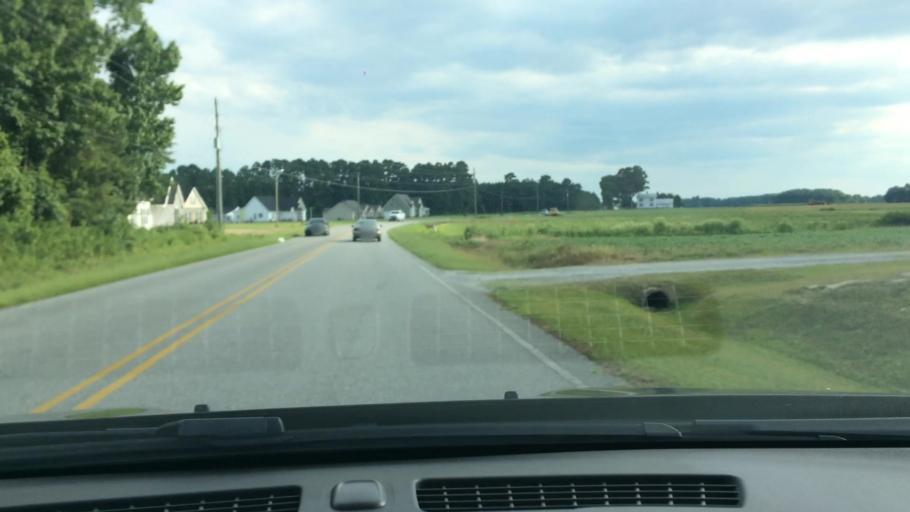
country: US
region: North Carolina
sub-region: Pitt County
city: Ayden
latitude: 35.4780
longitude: -77.3787
